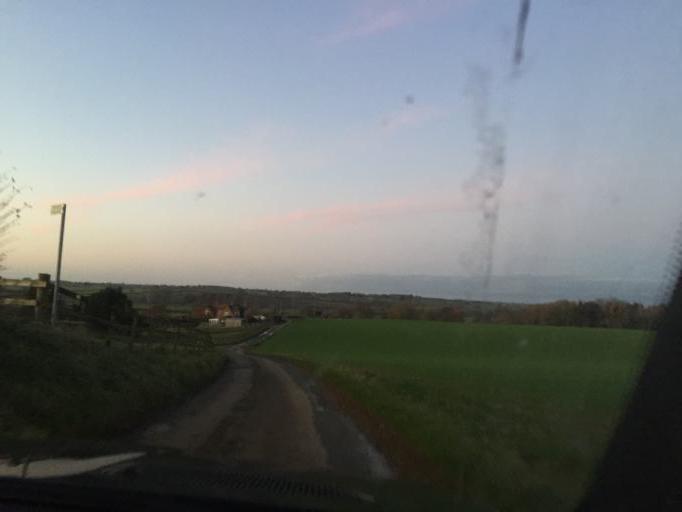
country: GB
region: England
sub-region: Northamptonshire
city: Brackley
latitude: 52.0905
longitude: -1.1112
